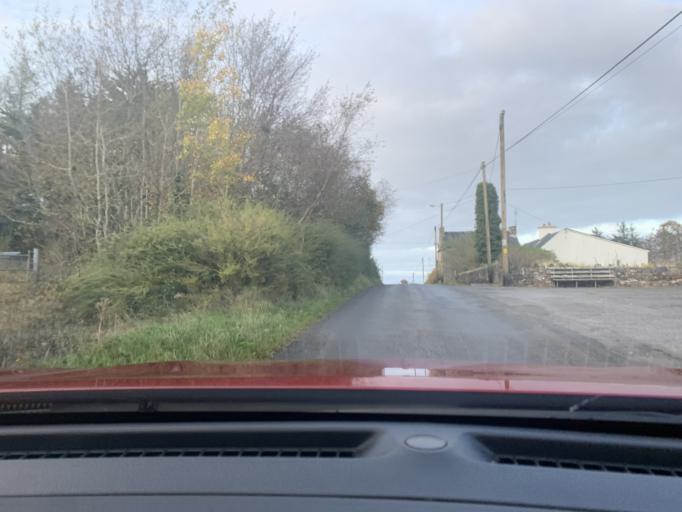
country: IE
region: Connaught
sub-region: Roscommon
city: Ballaghaderreen
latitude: 53.9748
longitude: -8.6210
